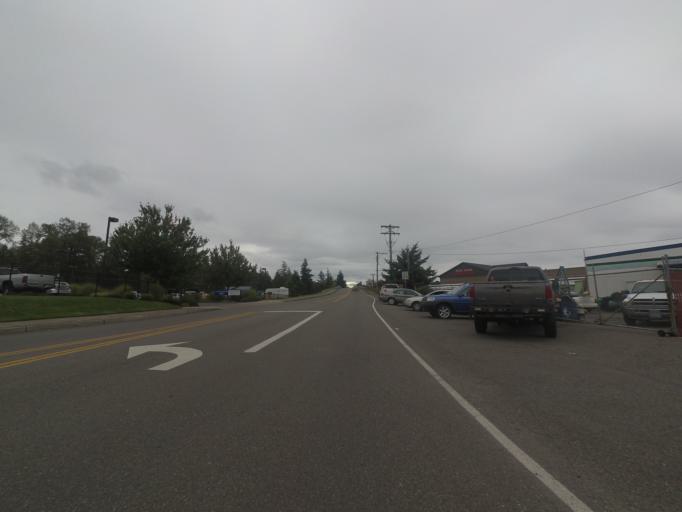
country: US
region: Washington
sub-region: Pierce County
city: McChord Air Force Base
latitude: 47.1518
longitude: -122.4991
